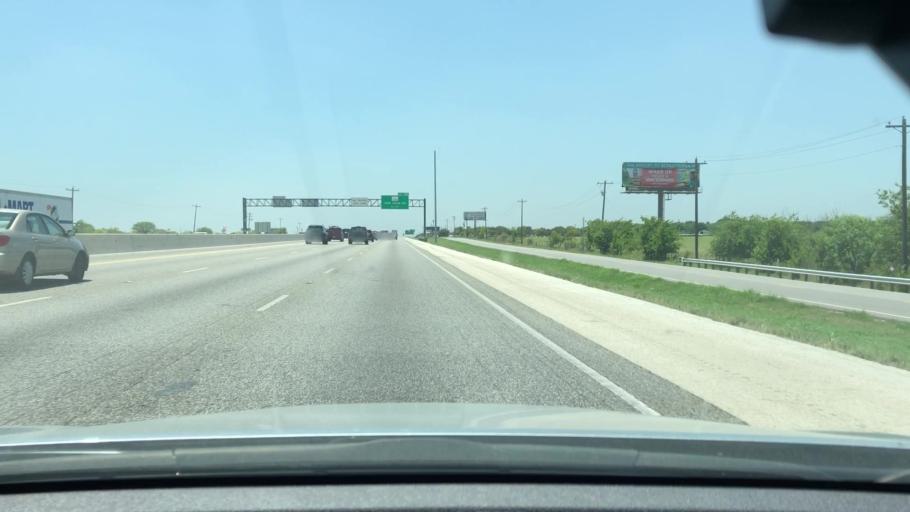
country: US
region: Texas
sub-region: Guadalupe County
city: Redwood
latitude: 29.8073
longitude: -98.0088
